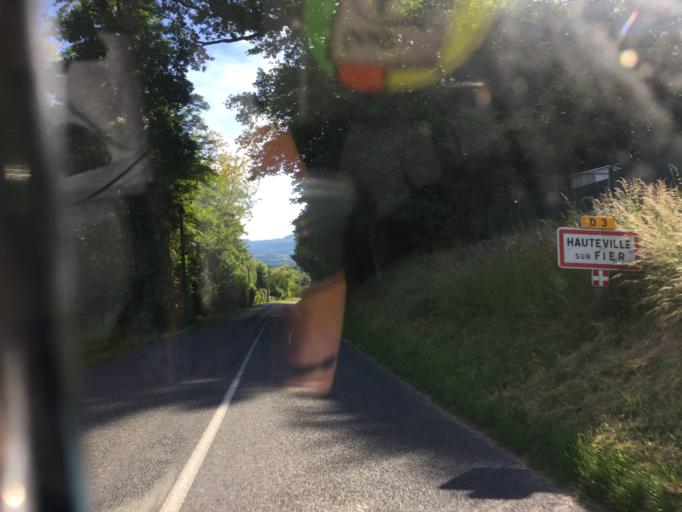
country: FR
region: Rhone-Alpes
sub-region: Departement de la Haute-Savoie
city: Sales
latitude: 45.9055
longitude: 5.9778
